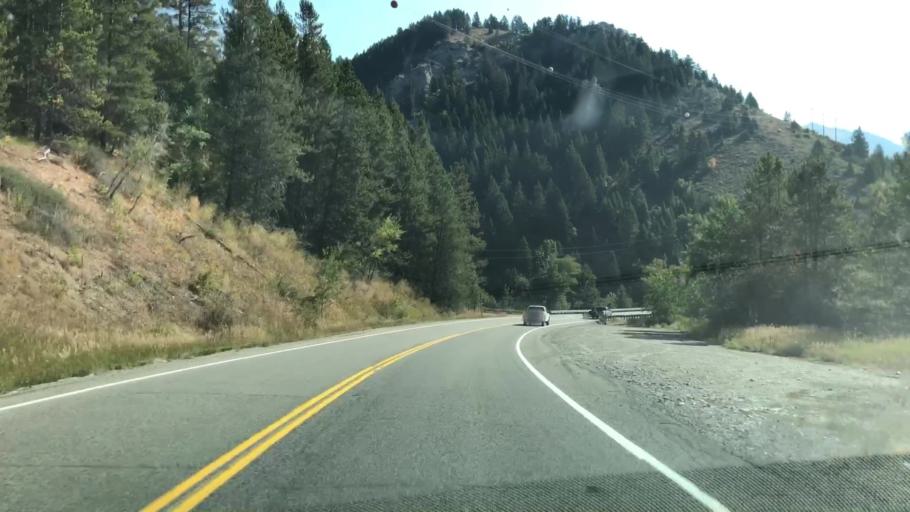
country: US
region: Idaho
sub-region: Teton County
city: Victor
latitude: 43.3202
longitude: -111.1599
